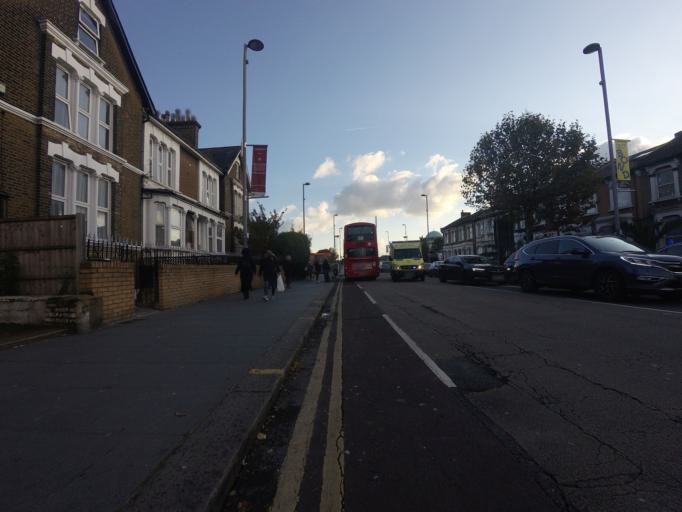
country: GB
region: England
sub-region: Greater London
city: Walthamstow
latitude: 51.5578
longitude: -0.0063
